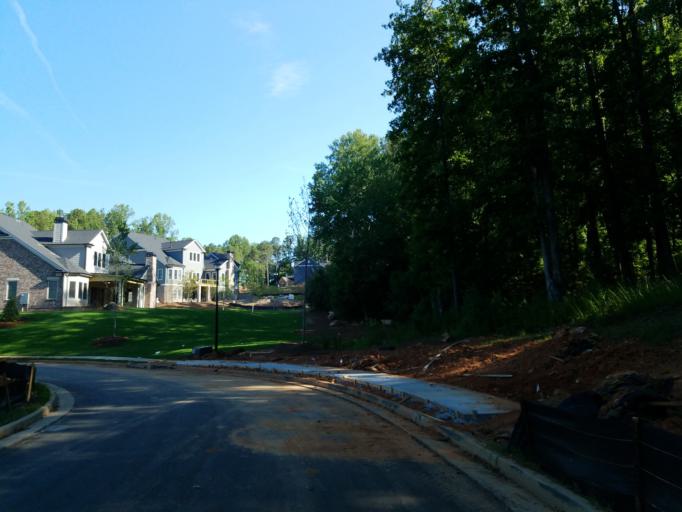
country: US
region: Georgia
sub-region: Fulton County
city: Milton
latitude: 34.1588
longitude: -84.3425
